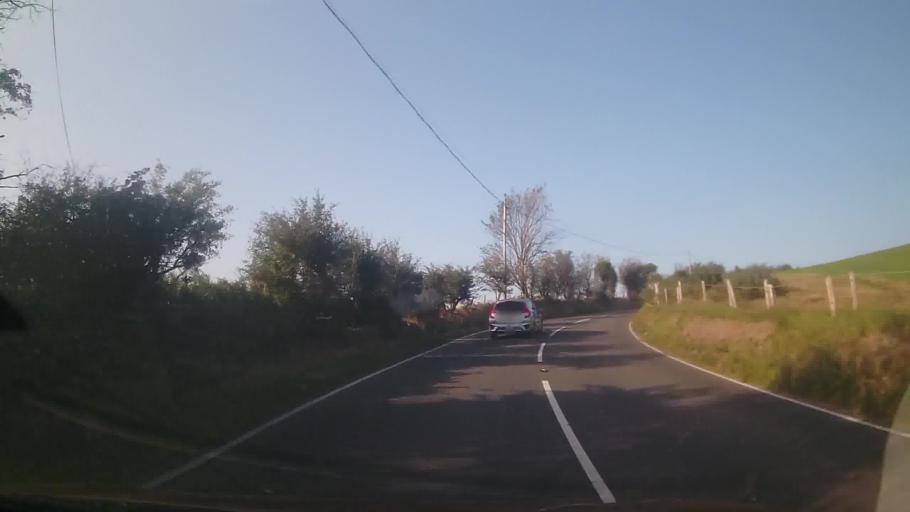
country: GB
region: Wales
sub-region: County of Ceredigion
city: Lledrod
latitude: 52.2900
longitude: -3.8617
